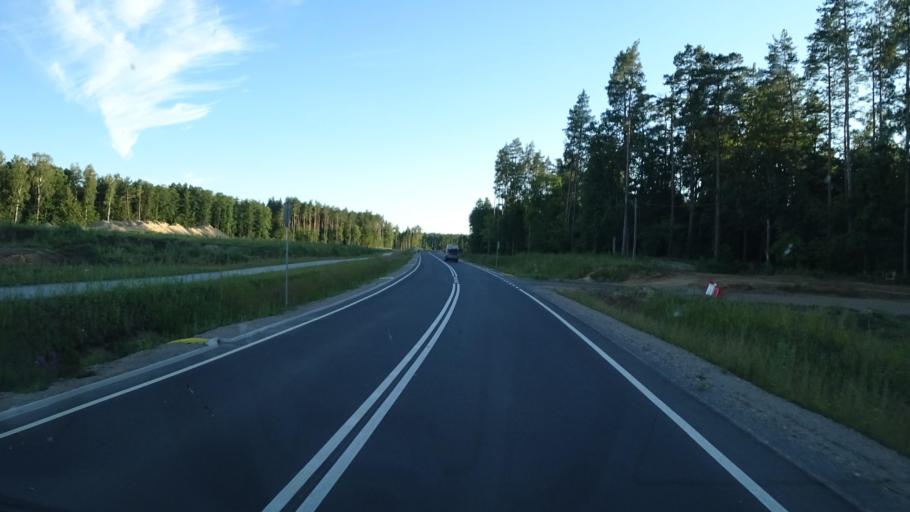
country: PL
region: Warmian-Masurian Voivodeship
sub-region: Powiat elcki
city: Elk
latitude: 53.8475
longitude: 22.4571
